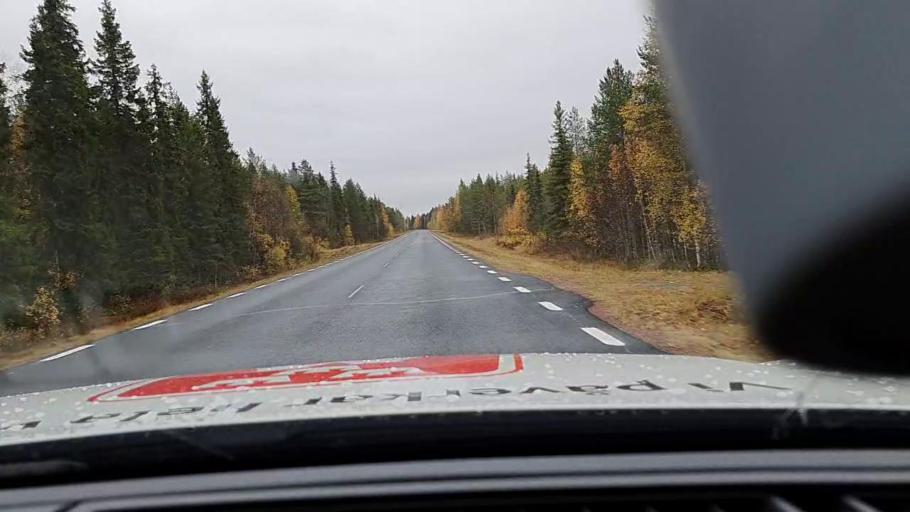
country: FI
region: Lapland
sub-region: Torniolaakso
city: Ylitornio
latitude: 66.1542
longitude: 23.8739
